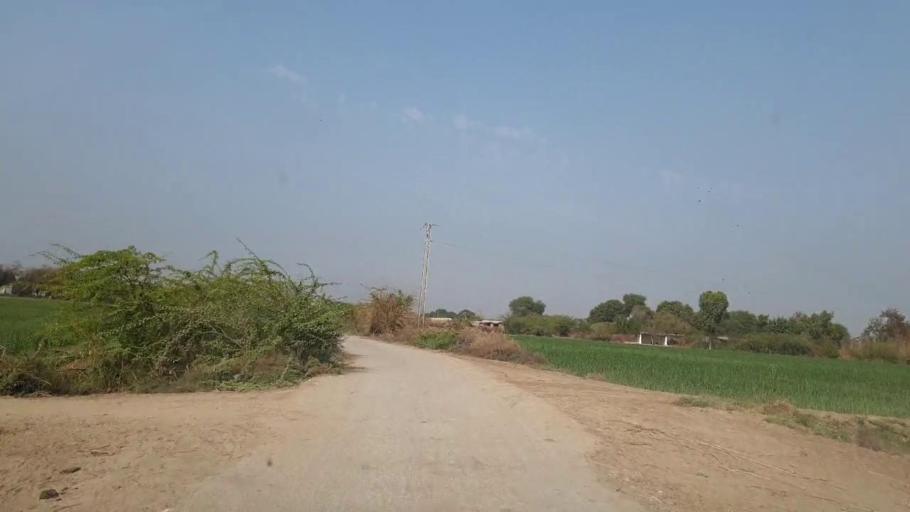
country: PK
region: Sindh
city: Mirpur Khas
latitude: 25.5702
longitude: 69.1522
